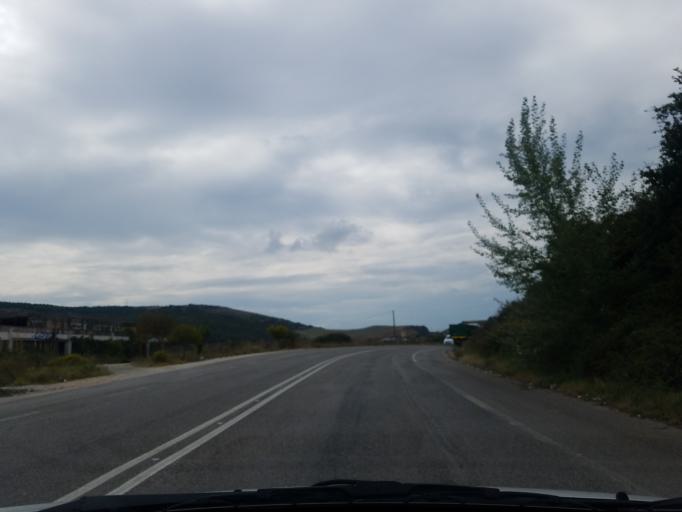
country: GR
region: Central Greece
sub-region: Nomos Fthiotidos
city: Domokos
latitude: 39.1146
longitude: 22.3103
